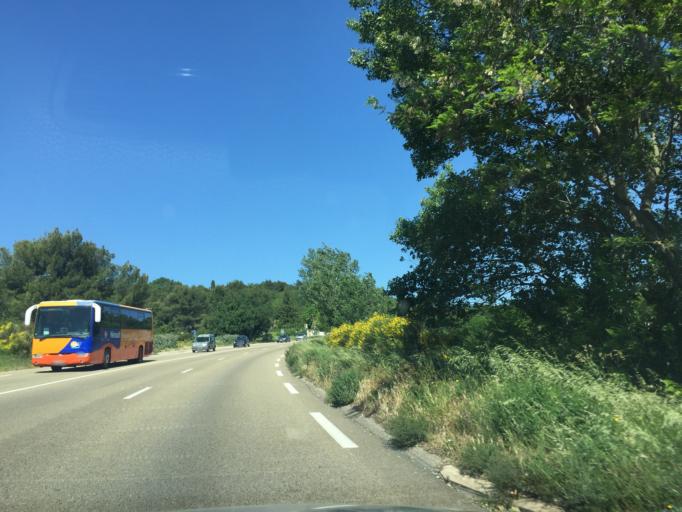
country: FR
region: Languedoc-Roussillon
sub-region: Departement du Gard
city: Saze
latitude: 43.9467
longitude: 4.6781
